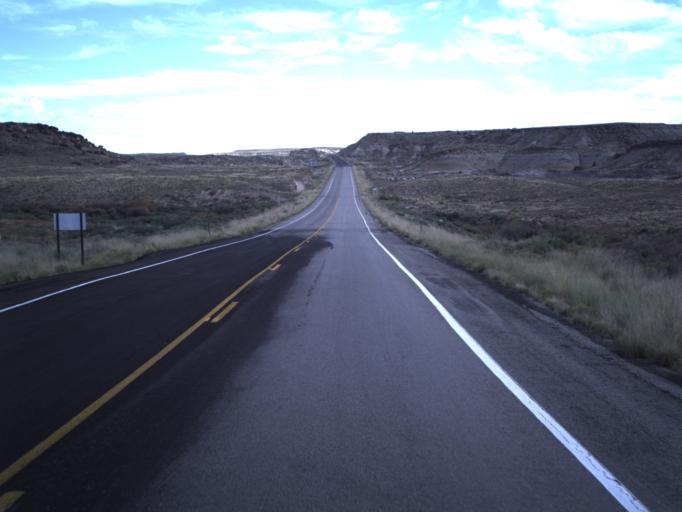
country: US
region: Colorado
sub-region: Montezuma County
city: Towaoc
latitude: 37.1545
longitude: -109.0507
